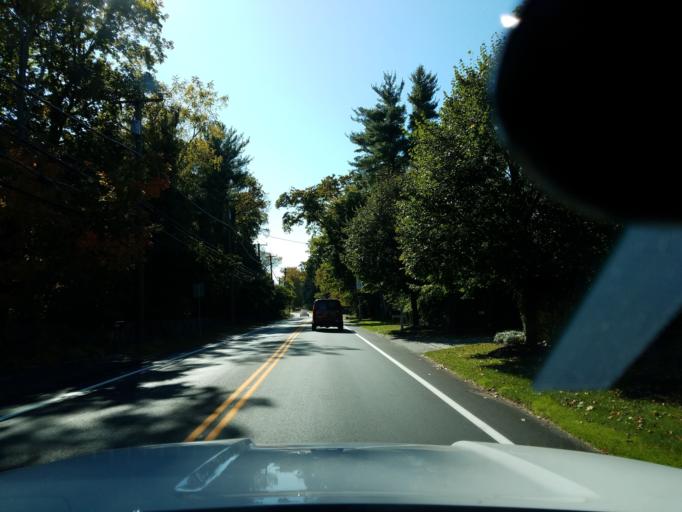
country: US
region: Connecticut
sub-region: Fairfield County
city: Cos Cob
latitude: 41.0721
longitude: -73.6233
